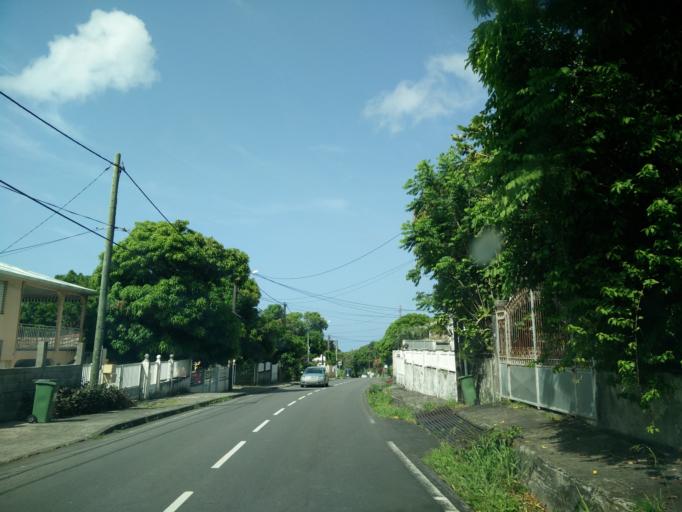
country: GP
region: Guadeloupe
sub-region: Guadeloupe
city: Gourbeyre
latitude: 15.9913
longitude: -61.7082
